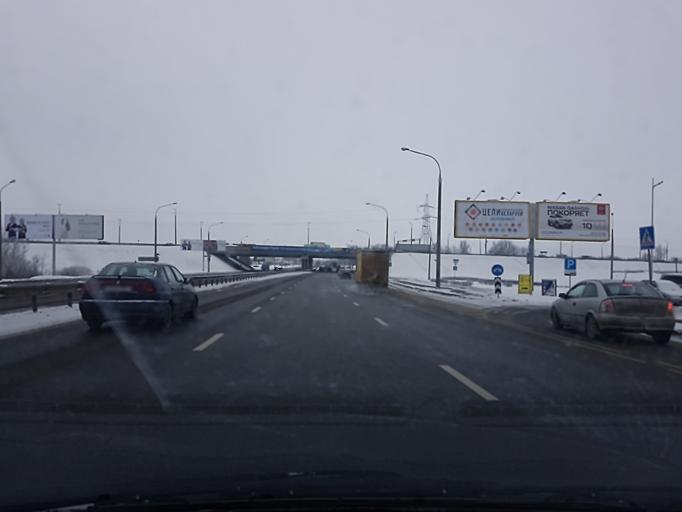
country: BY
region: Minsk
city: Shchomyslitsa
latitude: 53.8441
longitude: 27.4707
